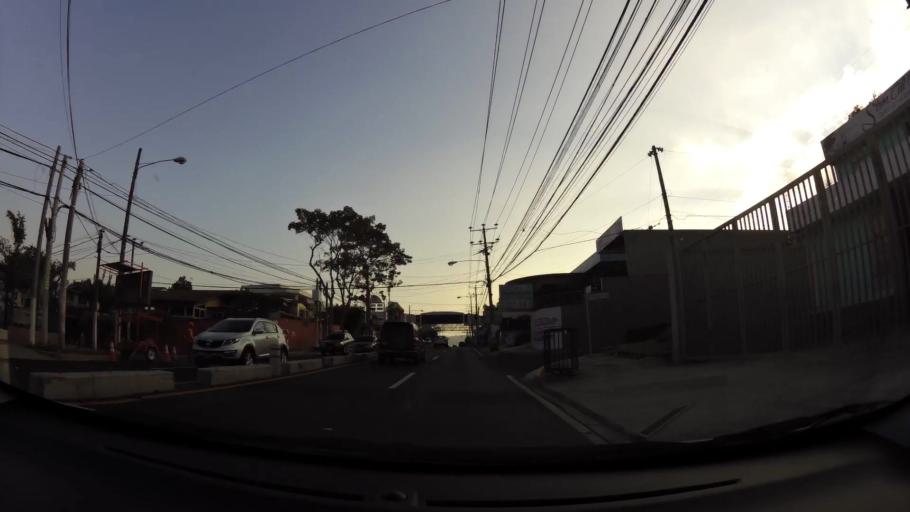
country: SV
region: La Libertad
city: Antiguo Cuscatlan
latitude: 13.6984
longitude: -89.2499
